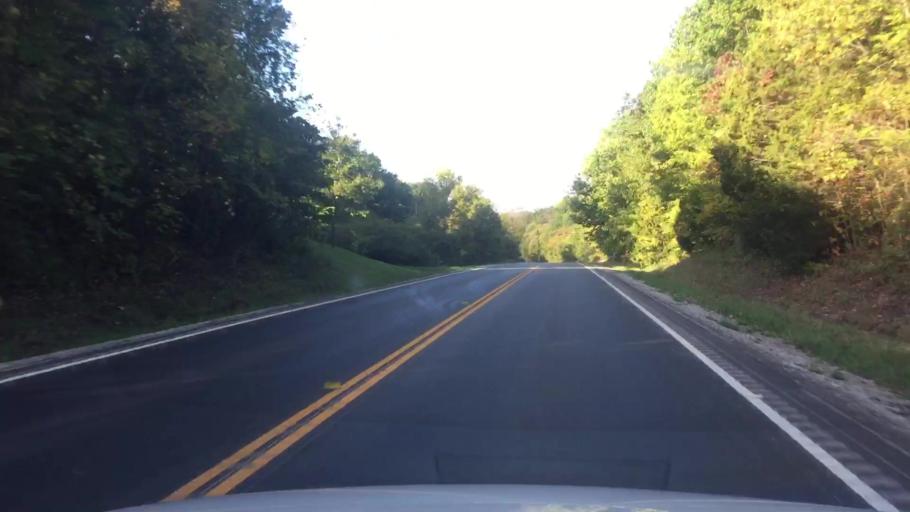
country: US
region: Missouri
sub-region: Howard County
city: New Franklin
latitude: 38.9950
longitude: -92.6089
